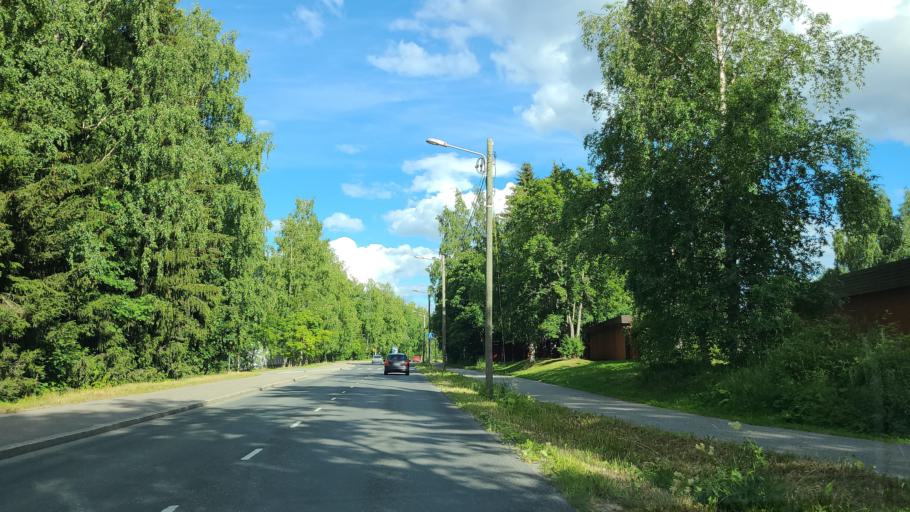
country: FI
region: Northern Savo
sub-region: Kuopio
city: Kuopio
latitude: 62.9374
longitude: 27.6535
